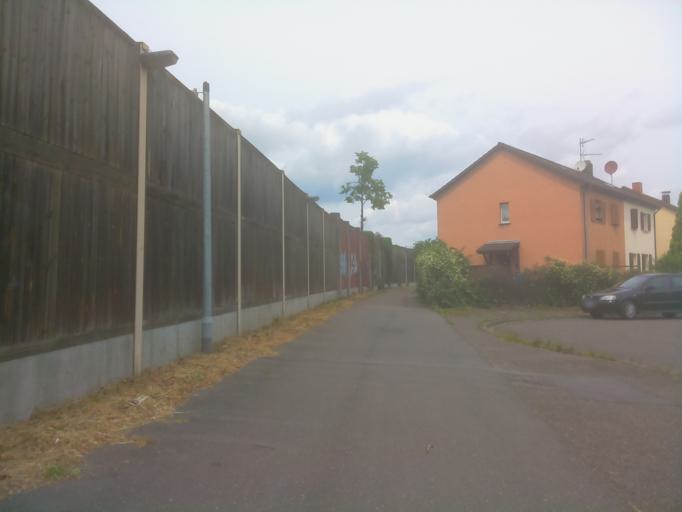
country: DE
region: Hesse
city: Lampertheim
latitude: 49.5487
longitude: 8.4517
